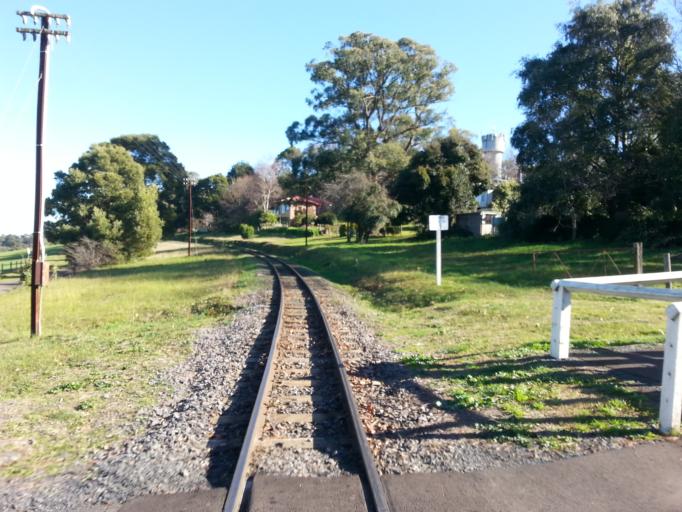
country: AU
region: Victoria
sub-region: Cardinia
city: Emerald
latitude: -37.9321
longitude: 145.4466
